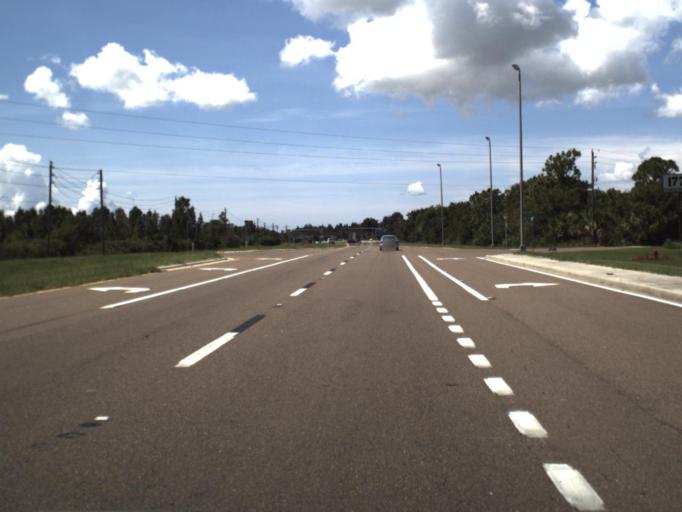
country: US
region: Florida
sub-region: Charlotte County
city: Cleveland
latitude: 26.9514
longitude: -81.9977
